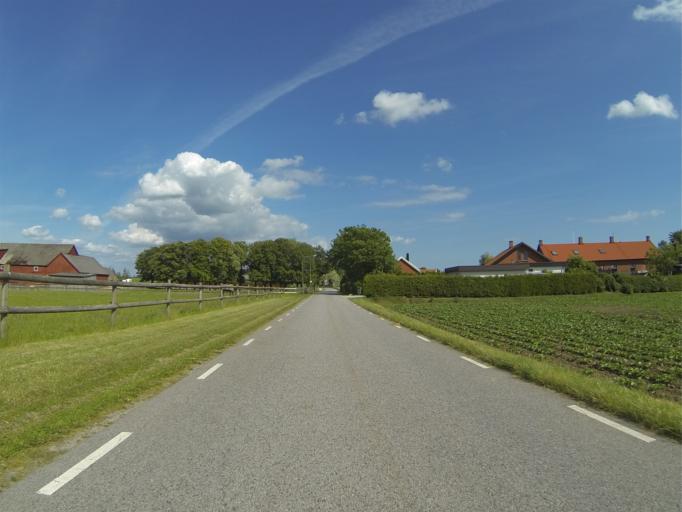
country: SE
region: Skane
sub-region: Staffanstorps Kommun
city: Hjaerup
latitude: 55.6314
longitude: 13.1350
